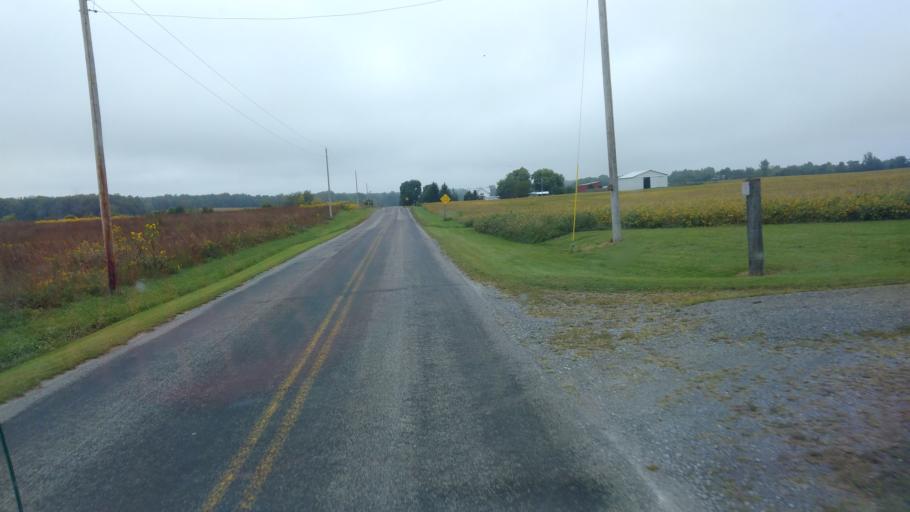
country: US
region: Ohio
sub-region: Hardin County
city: Kenton
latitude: 40.5603
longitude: -83.6364
